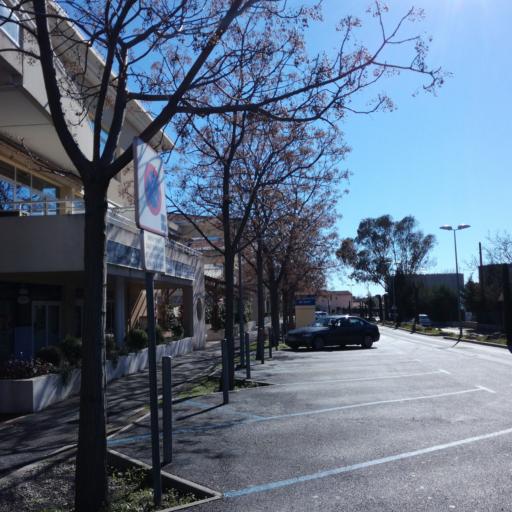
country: FR
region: Provence-Alpes-Cote d'Azur
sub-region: Departement des Alpes-Maritimes
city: Mouans-Sartoux
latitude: 43.6191
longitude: 6.9760
